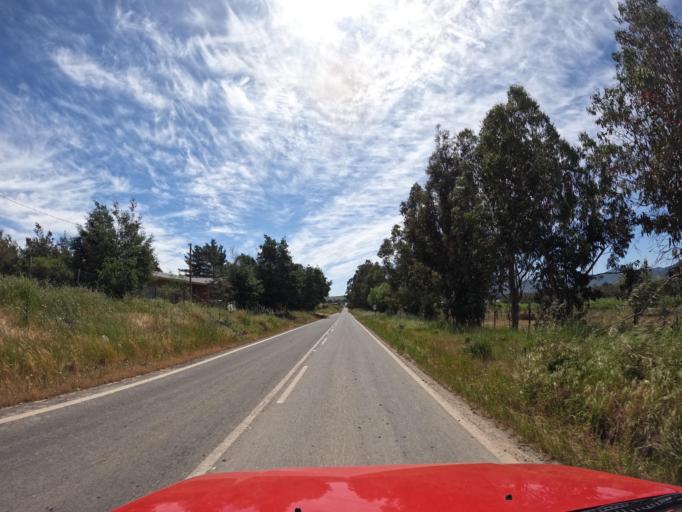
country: CL
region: Maule
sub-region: Provincia de Talca
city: Talca
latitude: -35.0387
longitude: -71.7552
